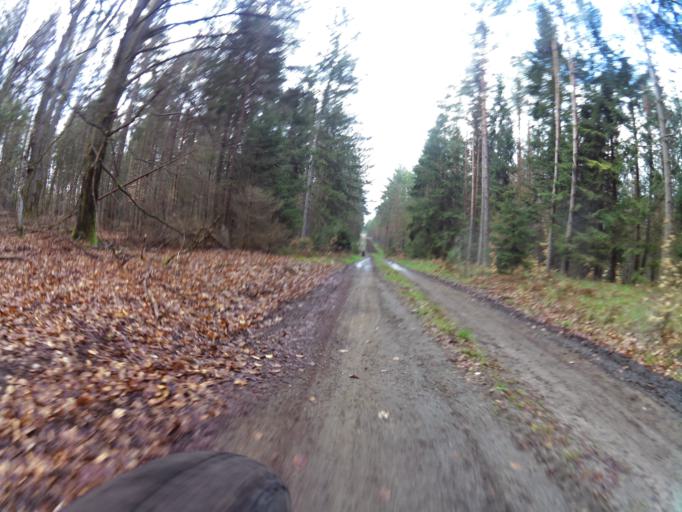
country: PL
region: Pomeranian Voivodeship
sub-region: Powiat slupski
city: Kepice
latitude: 54.3039
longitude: 16.8287
